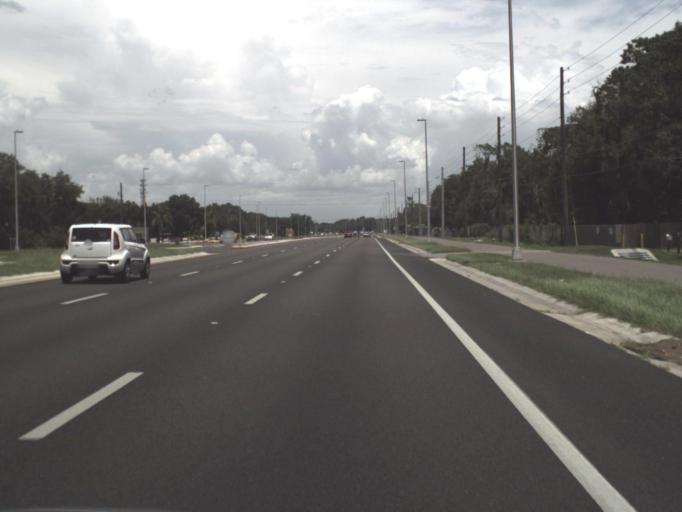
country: US
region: Florida
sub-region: Hillsborough County
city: Riverview
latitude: 27.8381
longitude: -82.3279
